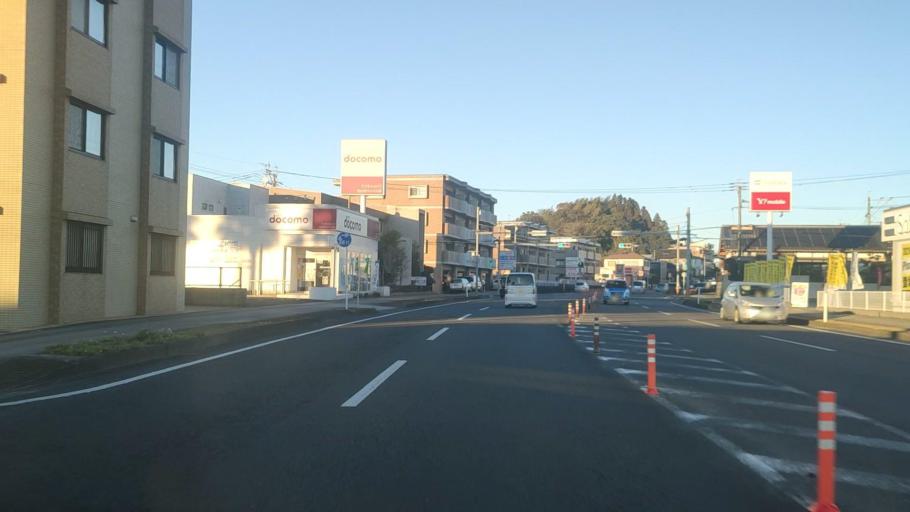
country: JP
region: Miyazaki
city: Miyazaki-shi
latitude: 31.9022
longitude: 131.4060
